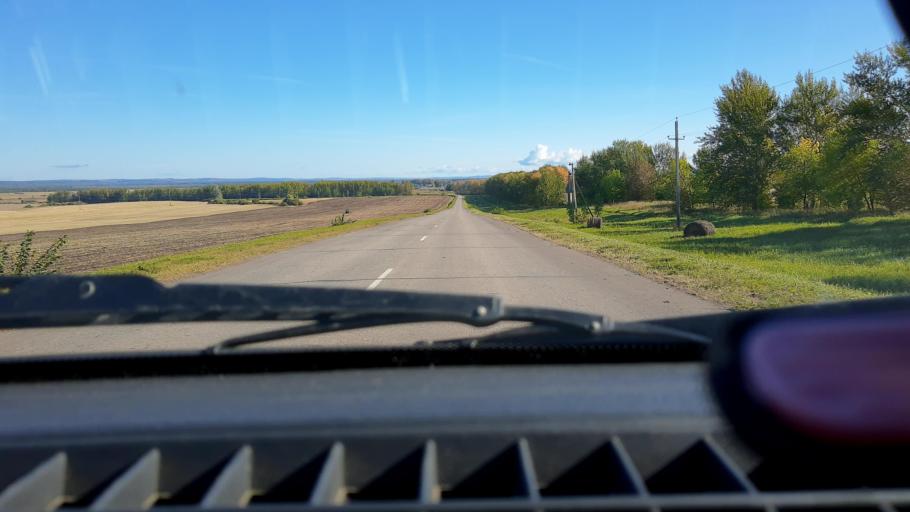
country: RU
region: Bashkortostan
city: Kushnarenkovo
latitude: 55.0775
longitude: 55.4644
